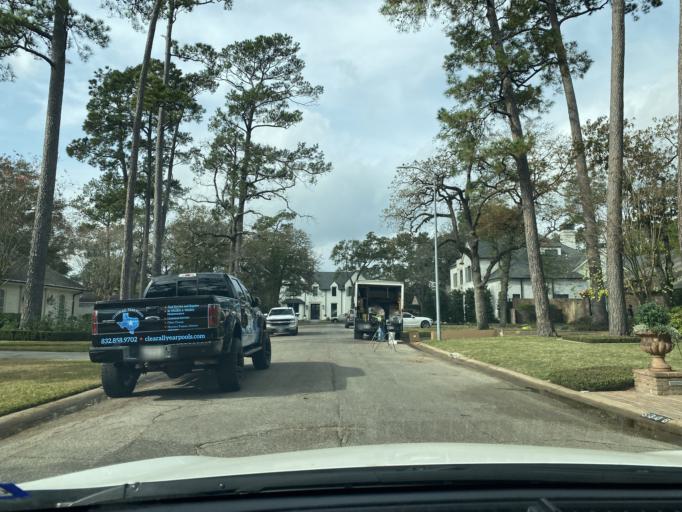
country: US
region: Texas
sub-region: Harris County
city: Hunters Creek Village
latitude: 29.7654
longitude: -95.4700
